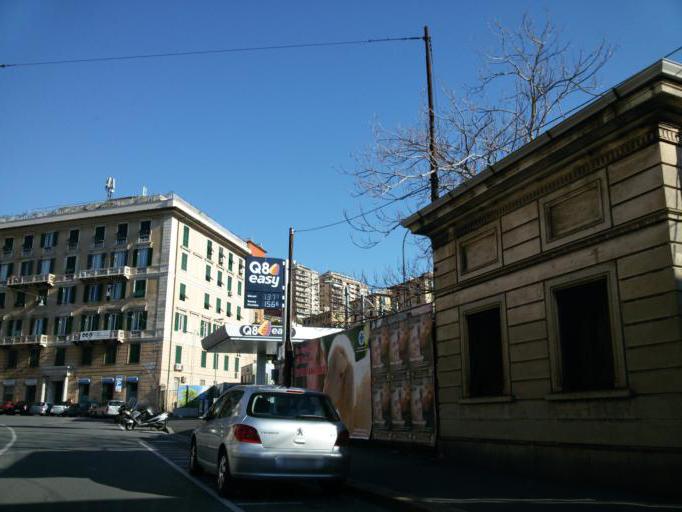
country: IT
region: Liguria
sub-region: Provincia di Genova
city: Genoa
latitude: 44.4086
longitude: 8.9445
